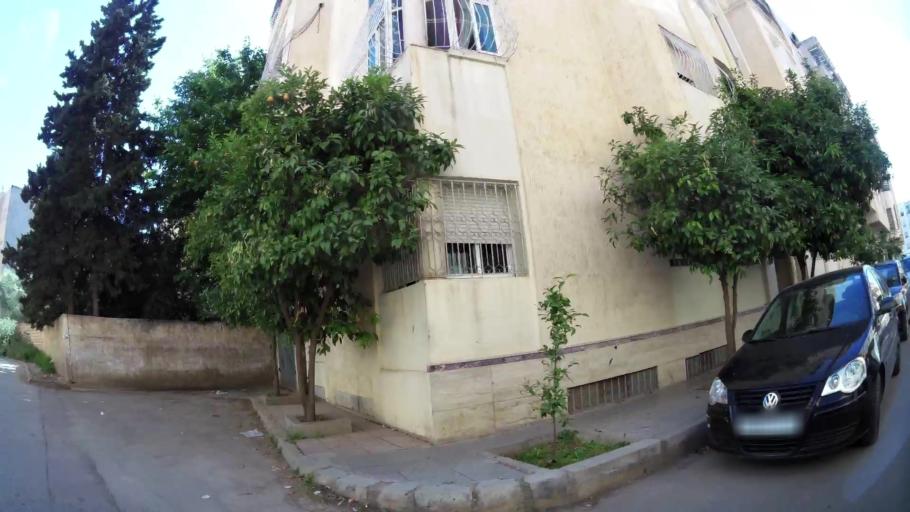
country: MA
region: Fes-Boulemane
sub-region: Fes
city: Fes
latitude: 34.0261
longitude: -4.9931
